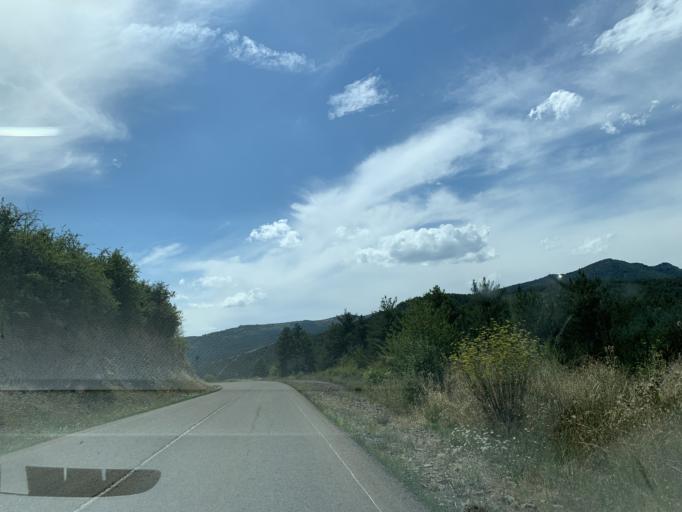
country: ES
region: Aragon
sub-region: Provincia de Huesca
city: Borau
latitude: 42.6628
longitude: -0.6273
